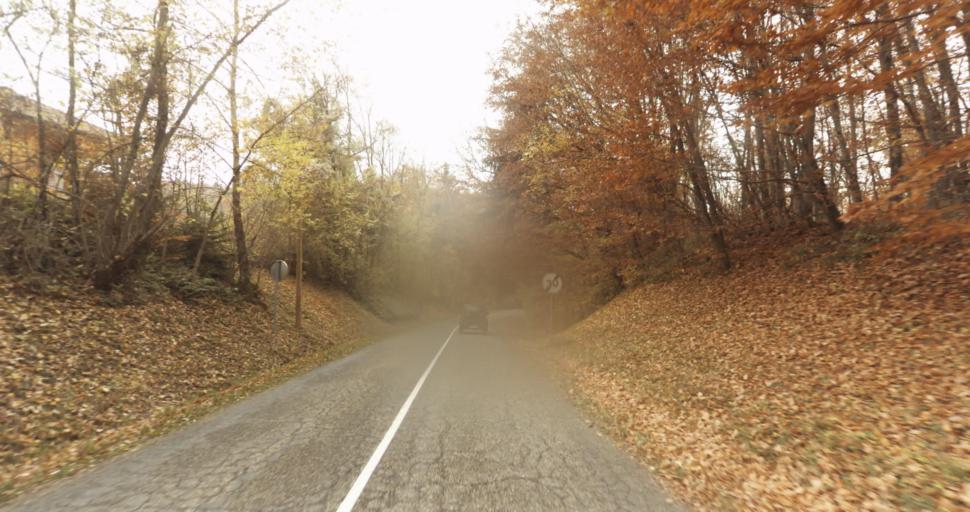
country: FR
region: Rhone-Alpes
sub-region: Departement de la Haute-Savoie
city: Saint-Martin-Bellevue
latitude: 45.9885
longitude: 6.1546
